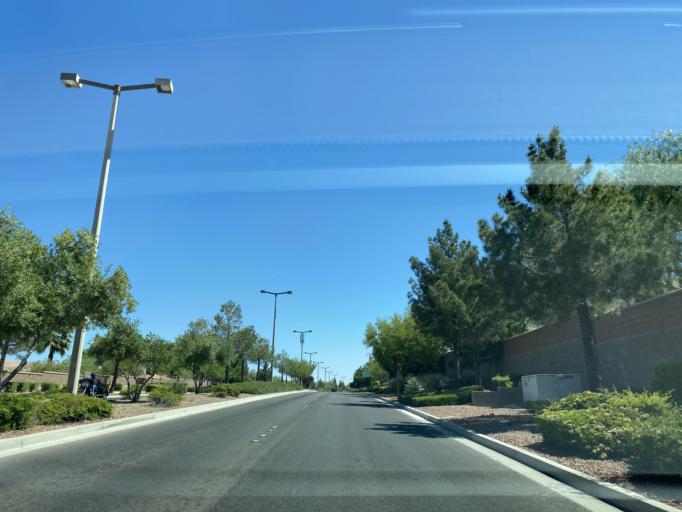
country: US
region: Nevada
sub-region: Clark County
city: Whitney
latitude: 35.9431
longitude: -115.1012
